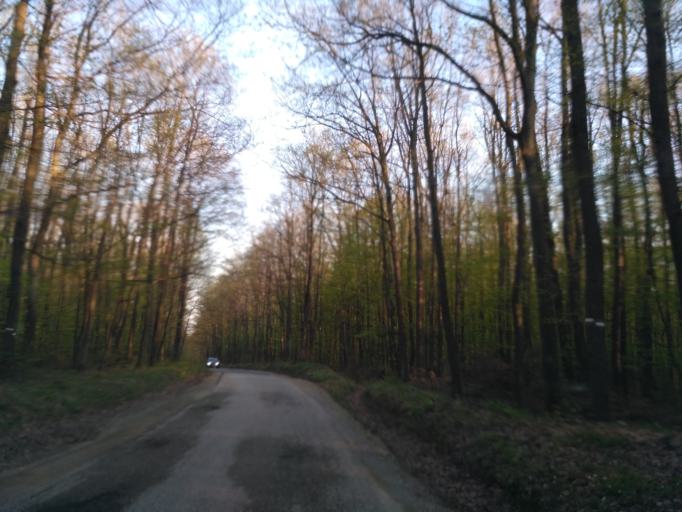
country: SK
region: Kosicky
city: Kosice
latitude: 48.7216
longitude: 21.1881
